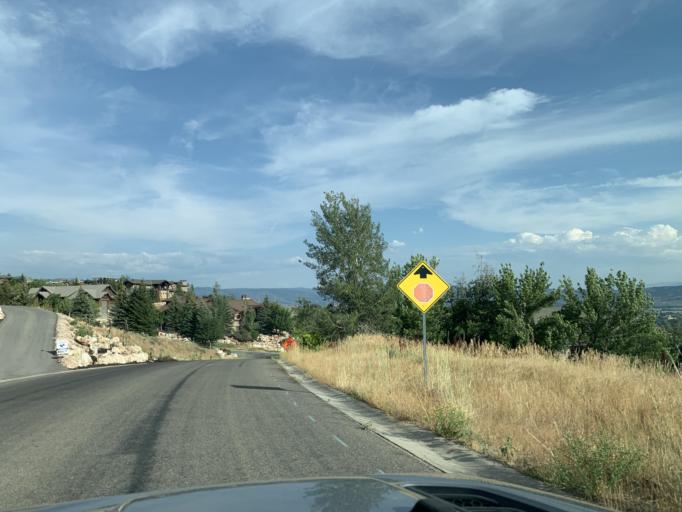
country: US
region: Utah
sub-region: Weber County
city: Wolf Creek
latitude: 41.3268
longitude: -111.8152
